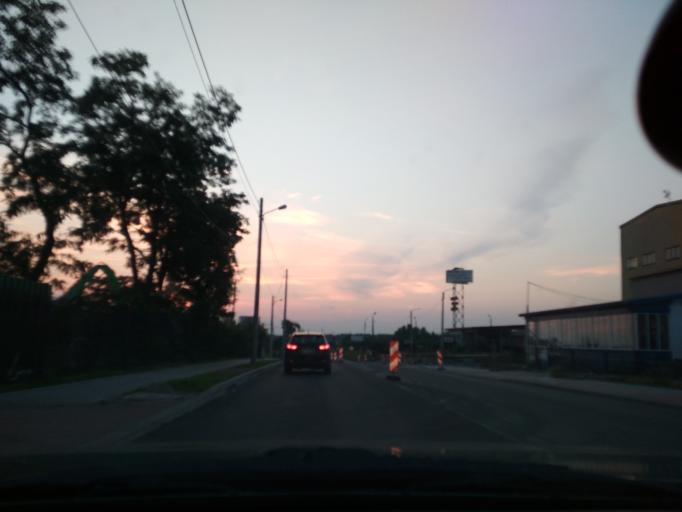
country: PL
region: Silesian Voivodeship
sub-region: Powiat zawiercianski
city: Ogrodzieniec
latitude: 50.4637
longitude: 19.4928
